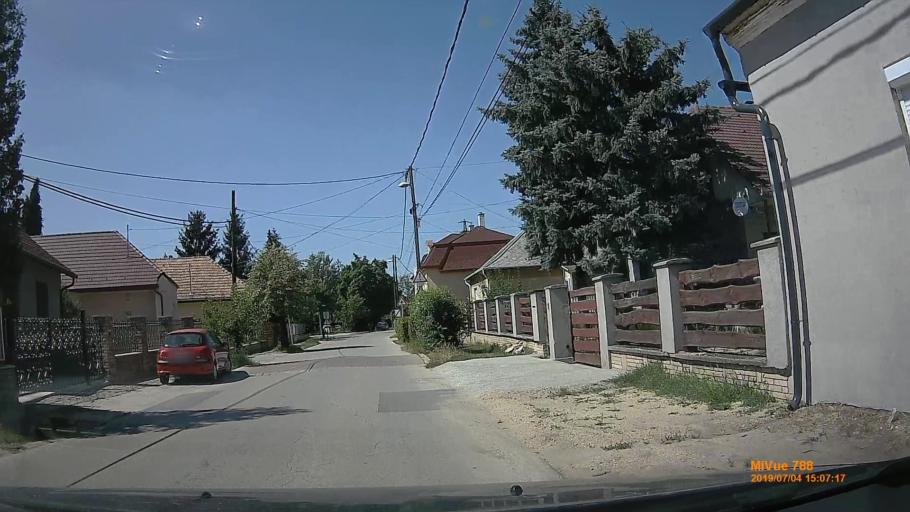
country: HU
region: Komarom-Esztergom
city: Tatabanya
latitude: 47.5734
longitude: 18.3919
